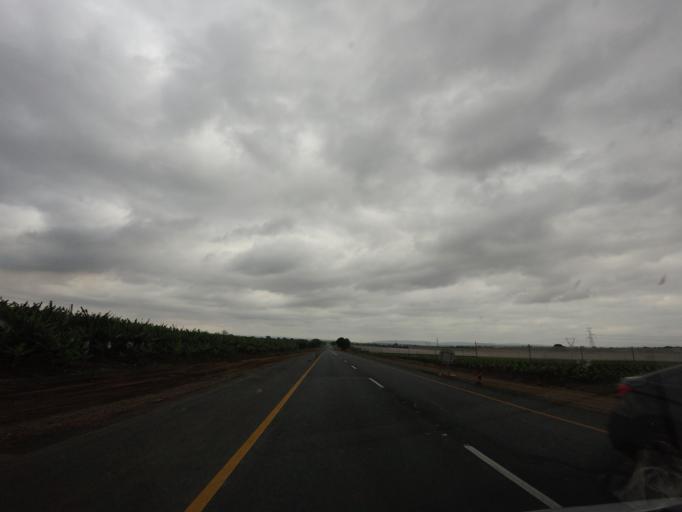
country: ZA
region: Mpumalanga
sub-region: Ehlanzeni District
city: Komatipoort
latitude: -25.4375
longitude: 31.7955
